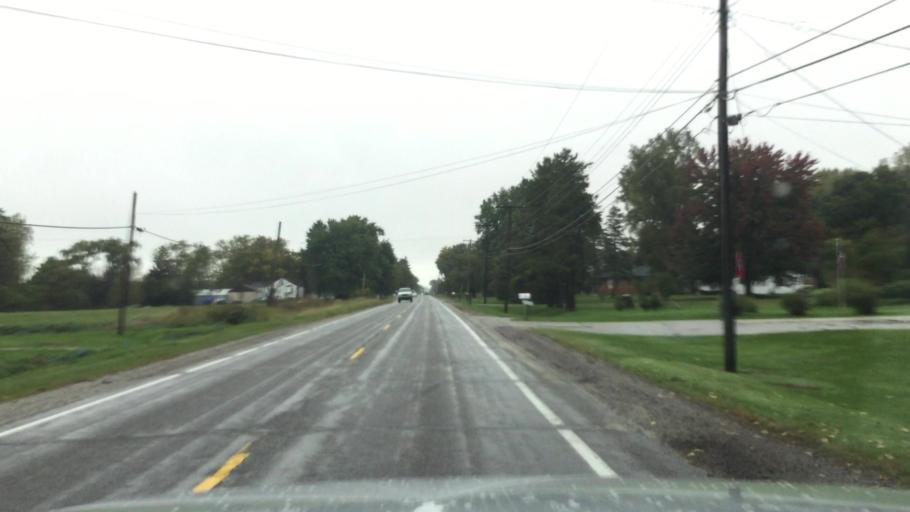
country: US
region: Michigan
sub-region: Saginaw County
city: Bridgeport
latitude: 43.3662
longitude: -83.9350
